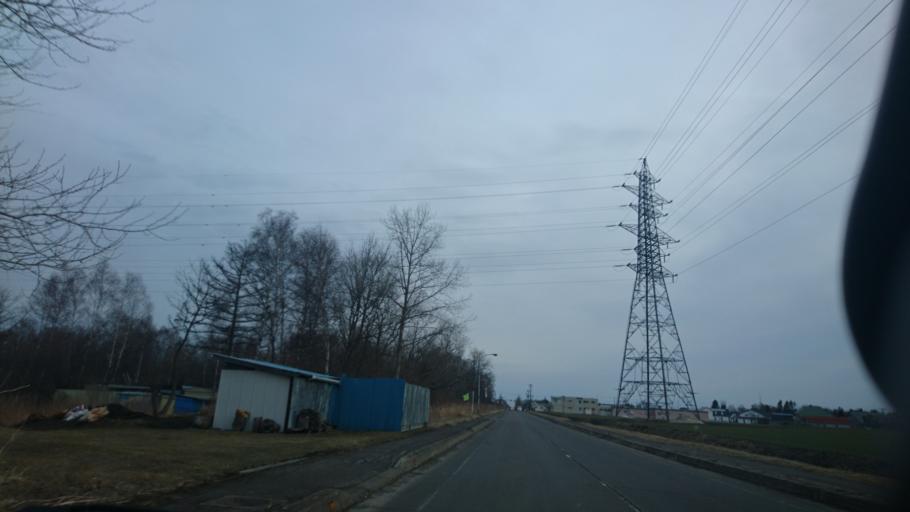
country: JP
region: Hokkaido
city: Otofuke
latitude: 42.9750
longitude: 143.1983
